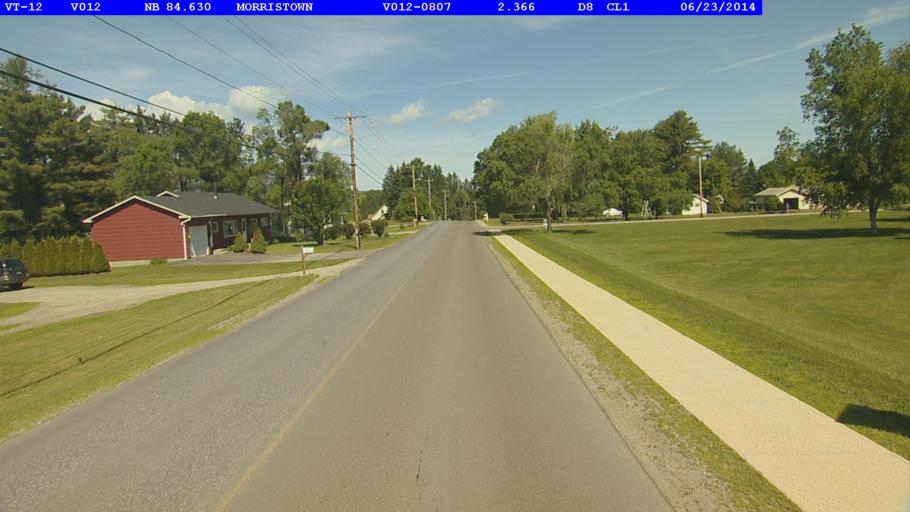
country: US
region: Vermont
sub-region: Lamoille County
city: Morrisville
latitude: 44.5555
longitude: -72.5811
